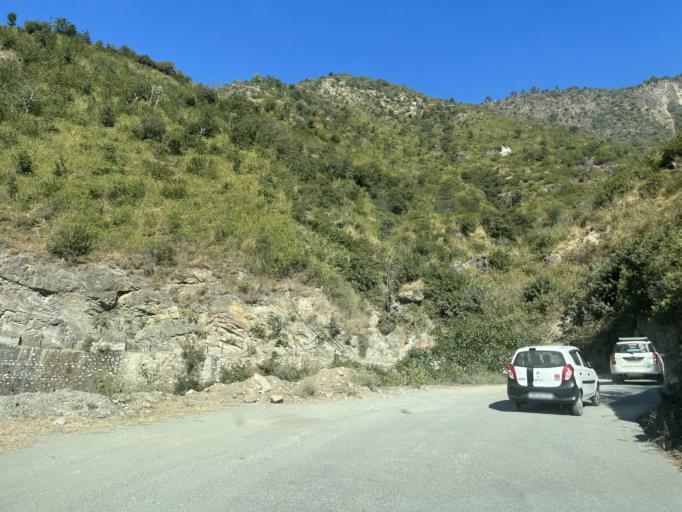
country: IN
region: Uttarakhand
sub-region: Naini Tal
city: Naini Tal
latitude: 29.5096
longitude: 79.4526
